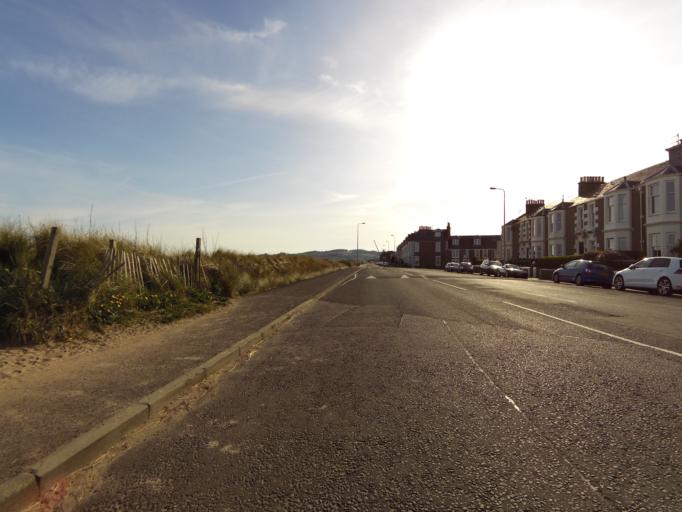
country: GB
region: Scotland
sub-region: Fife
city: Tayport
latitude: 56.4664
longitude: -2.8610
